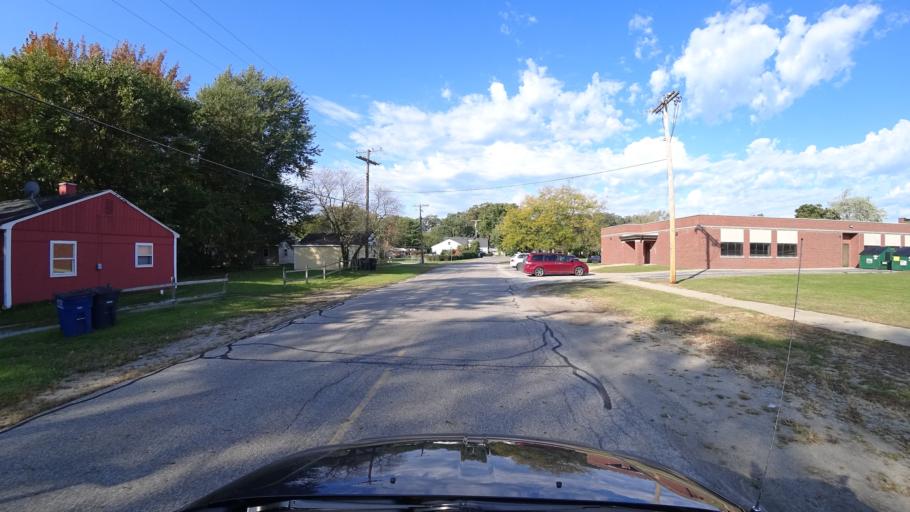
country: US
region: Indiana
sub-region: LaPorte County
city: Trail Creek
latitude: 41.7054
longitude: -86.8678
